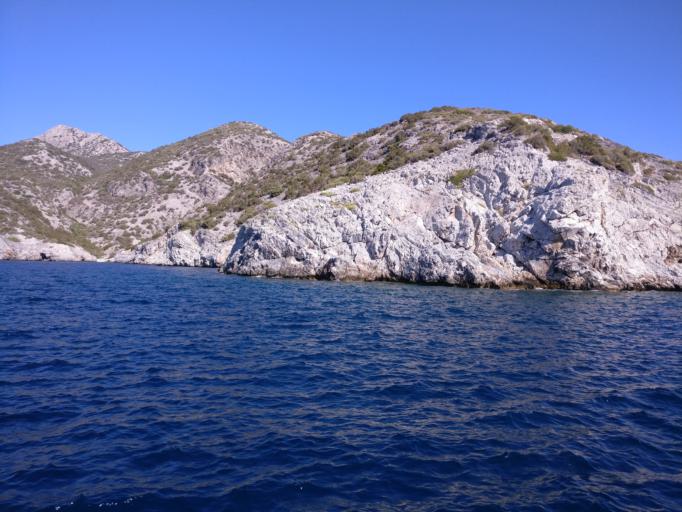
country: GR
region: North Aegean
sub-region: Nomos Samou
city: Chora
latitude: 37.6356
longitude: 26.8596
